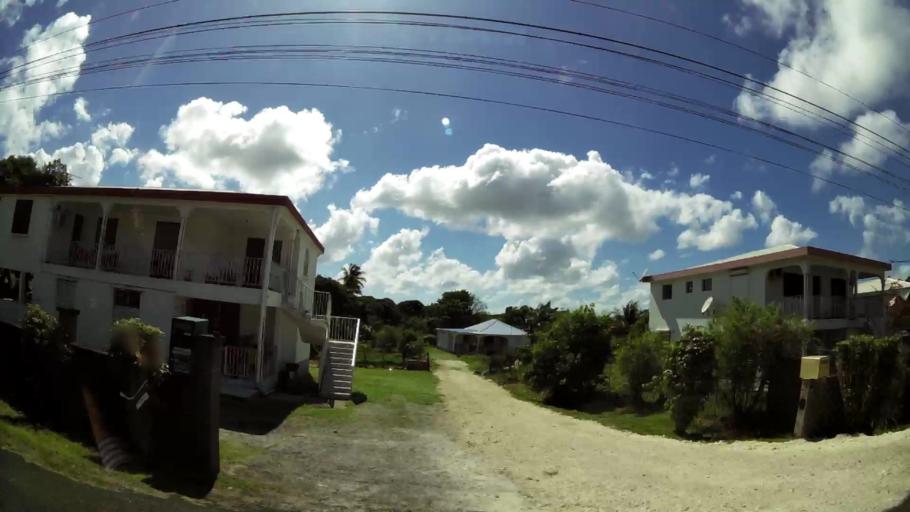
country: GP
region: Guadeloupe
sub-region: Guadeloupe
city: Petit-Canal
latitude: 16.3699
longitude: -61.4456
